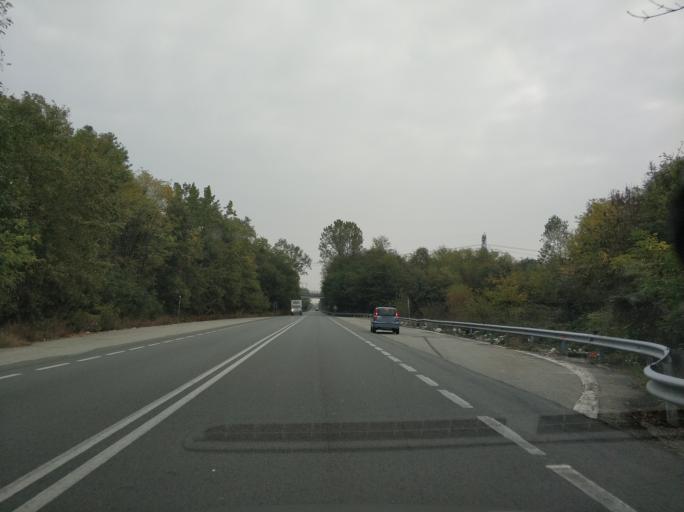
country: IT
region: Piedmont
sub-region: Provincia di Torino
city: Leini
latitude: 45.2093
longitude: 7.7178
